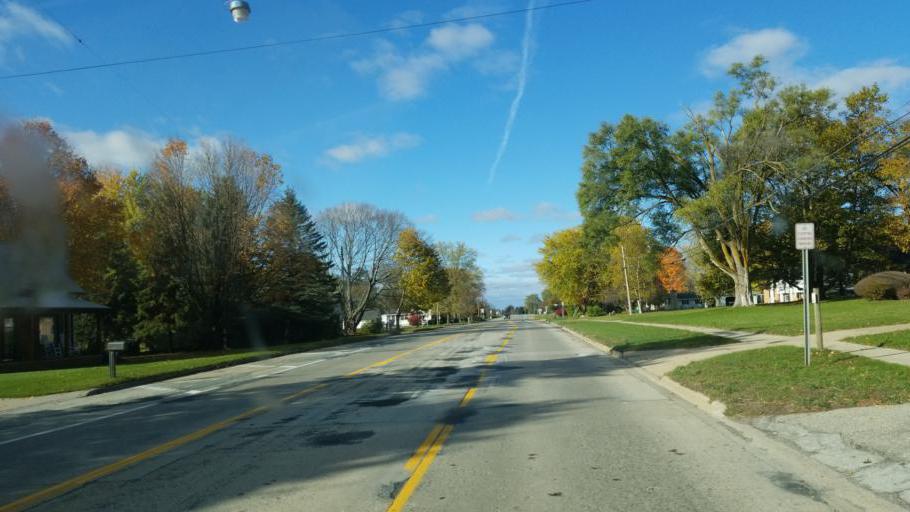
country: US
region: Michigan
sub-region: Montcalm County
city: Edmore
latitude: 43.4082
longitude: -85.0489
